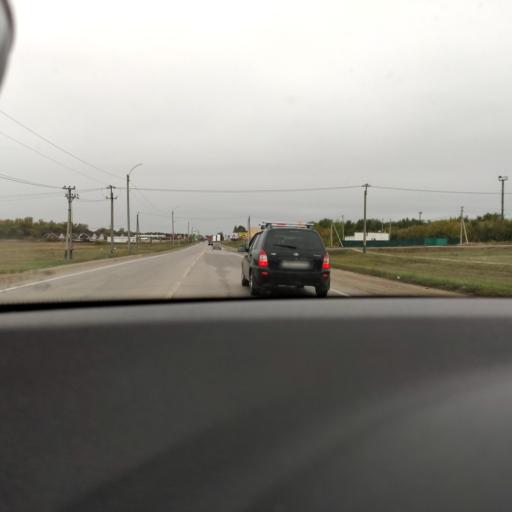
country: RU
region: Samara
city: Krasnyy Yar
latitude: 53.4838
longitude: 50.3908
